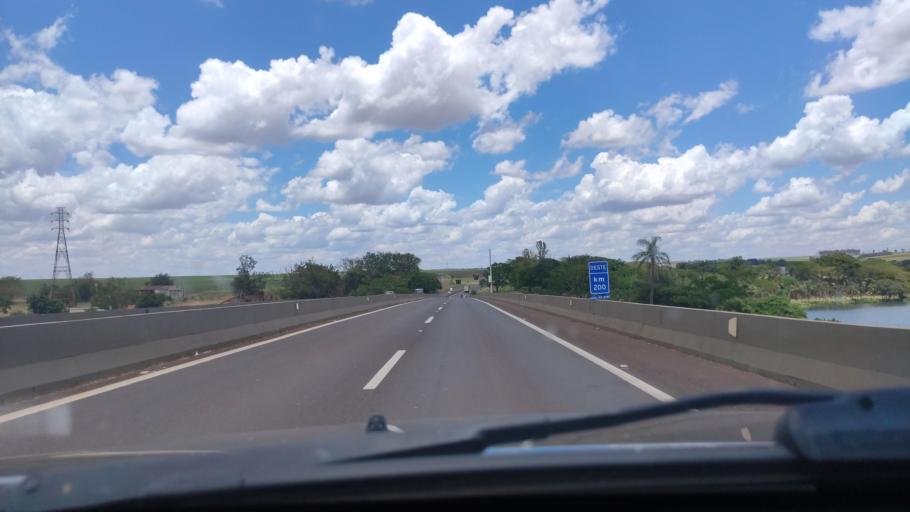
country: BR
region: Sao Paulo
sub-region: Pederneiras
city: Pederneiras
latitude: -22.3217
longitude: -48.7301
